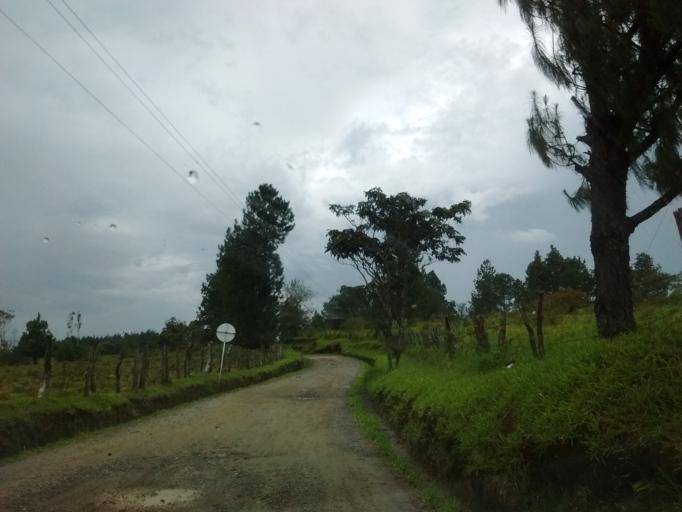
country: CO
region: Cauca
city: Cajibio
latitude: 2.5684
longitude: -76.6394
